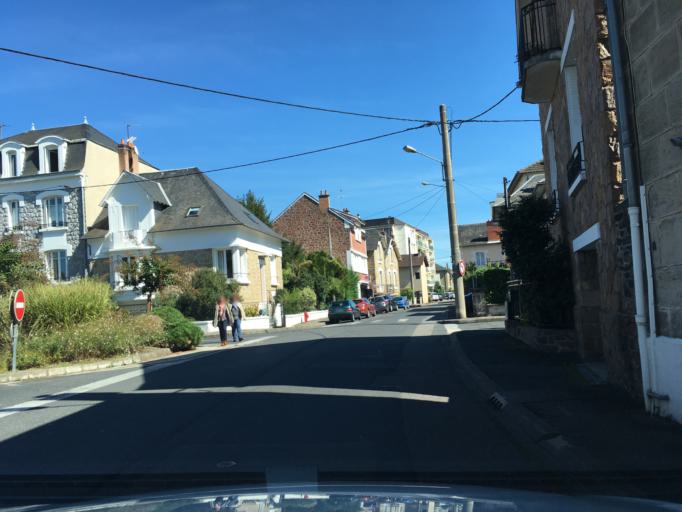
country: FR
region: Limousin
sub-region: Departement de la Correze
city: Brive-la-Gaillarde
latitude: 45.1614
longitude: 1.5377
